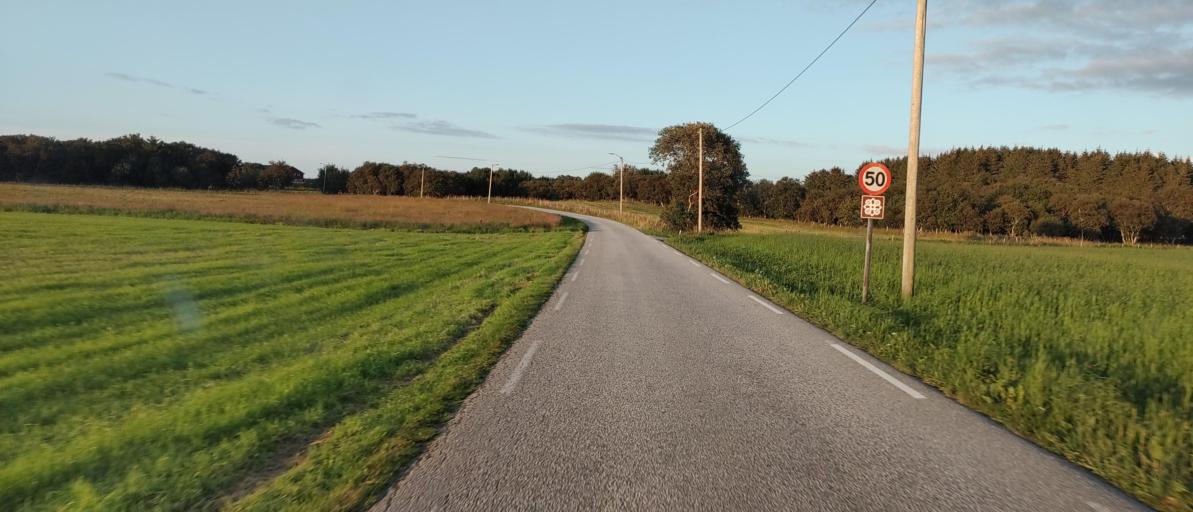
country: NO
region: More og Romsdal
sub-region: Fraena
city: Elnesvagen
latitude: 62.9912
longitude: 7.2171
